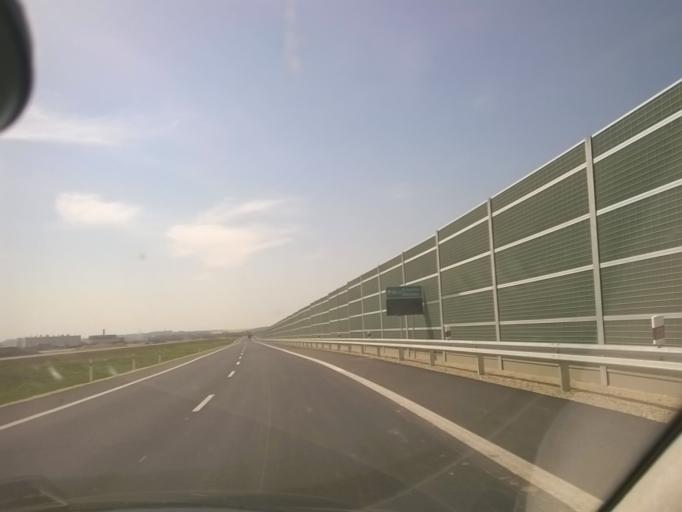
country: SK
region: Nitriansky
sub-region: Okres Nitra
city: Nitra
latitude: 48.3637
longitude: 18.0381
